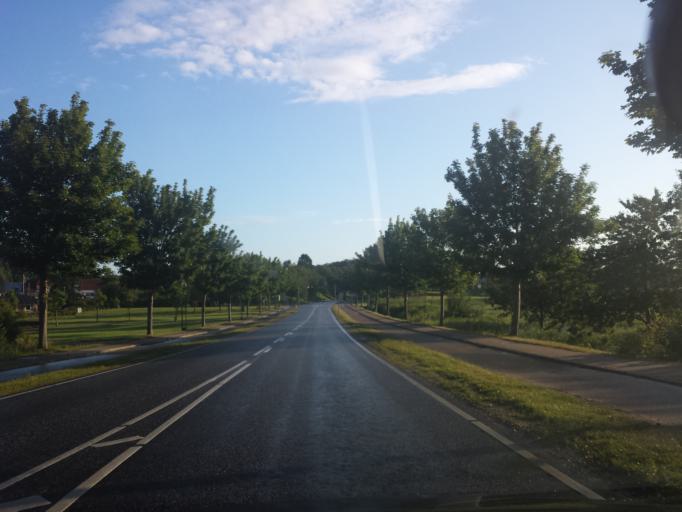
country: DK
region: South Denmark
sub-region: Sonderborg Kommune
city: Grasten
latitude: 54.9136
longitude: 9.5881
